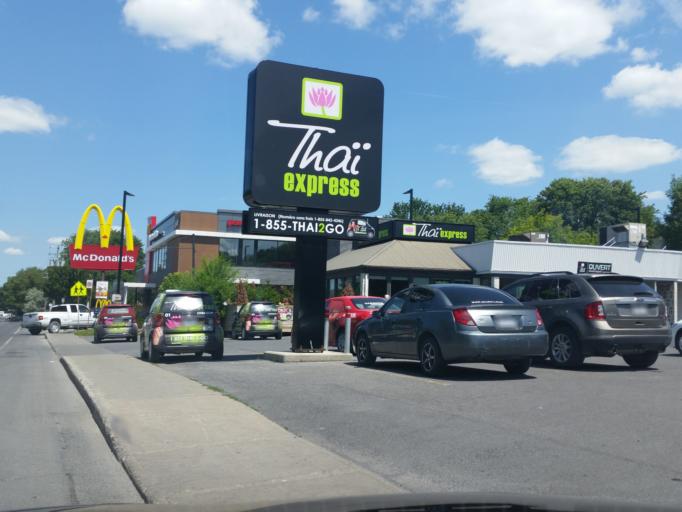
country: CA
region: Quebec
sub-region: Monteregie
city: Saint-Jean-sur-Richelieu
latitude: 45.3194
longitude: -73.2638
